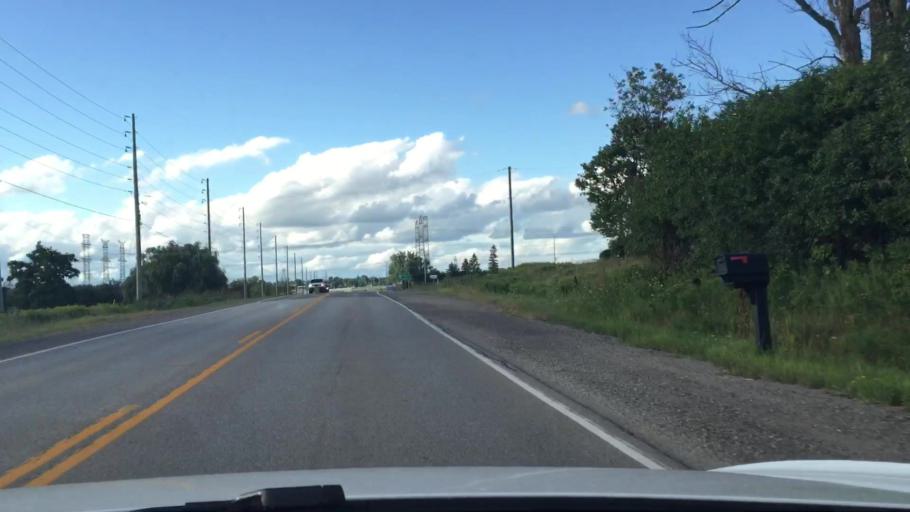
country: CA
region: Ontario
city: Oshawa
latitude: 43.9731
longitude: -78.8642
